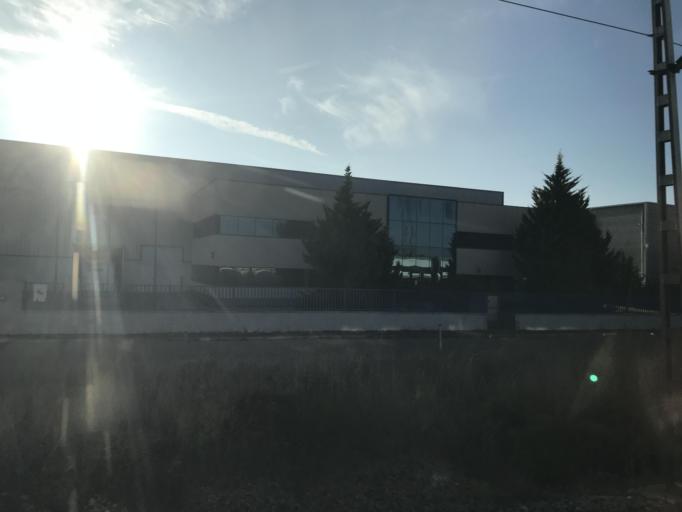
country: ES
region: Castille and Leon
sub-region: Provincia de Palencia
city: Duenas
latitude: 41.8532
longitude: -4.5518
